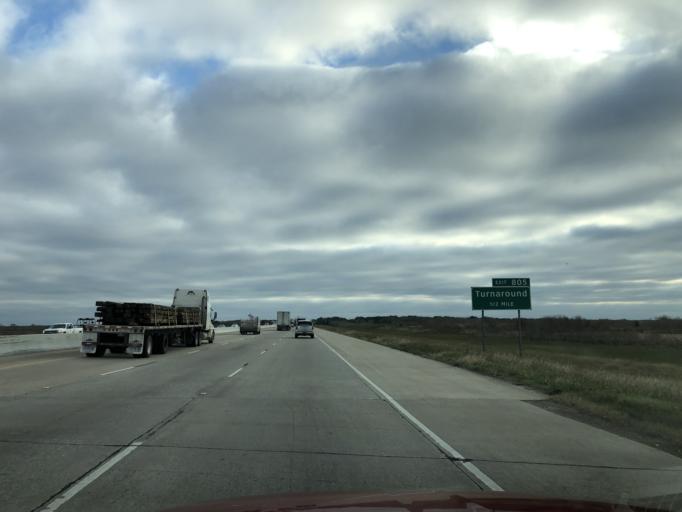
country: US
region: Texas
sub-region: Chambers County
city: Old River-Winfree
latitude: 29.8344
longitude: -94.7821
